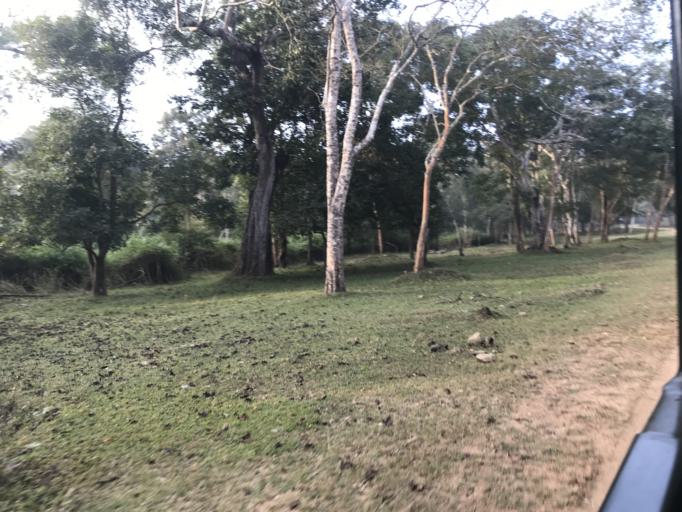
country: IN
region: Karnataka
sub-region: Mysore
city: Heggadadevankote
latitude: 12.0079
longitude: 76.2381
